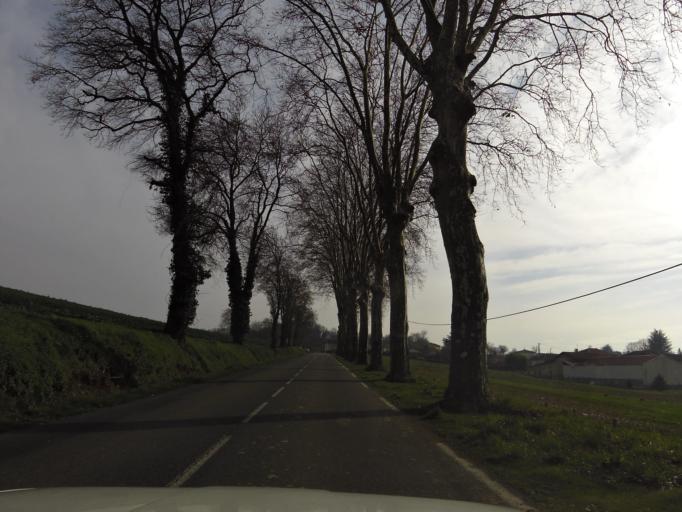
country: FR
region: Rhone-Alpes
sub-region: Departement de l'Ain
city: Chalamont
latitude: 46.0007
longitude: 5.1657
